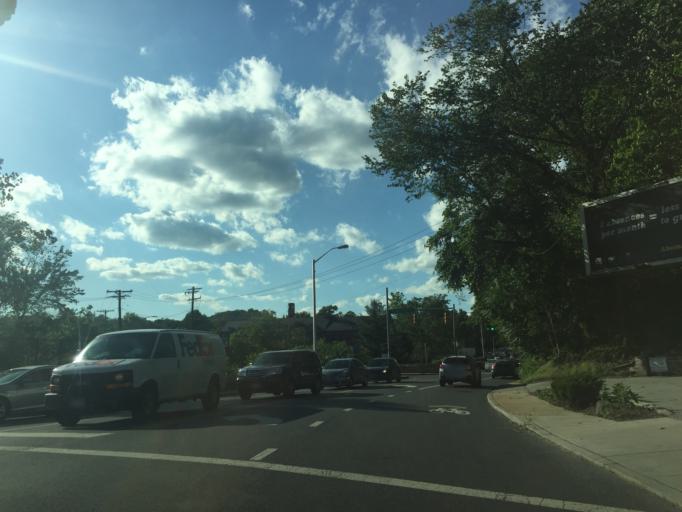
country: US
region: Maryland
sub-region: Baltimore County
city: Towson
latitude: 39.3672
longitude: -76.6481
